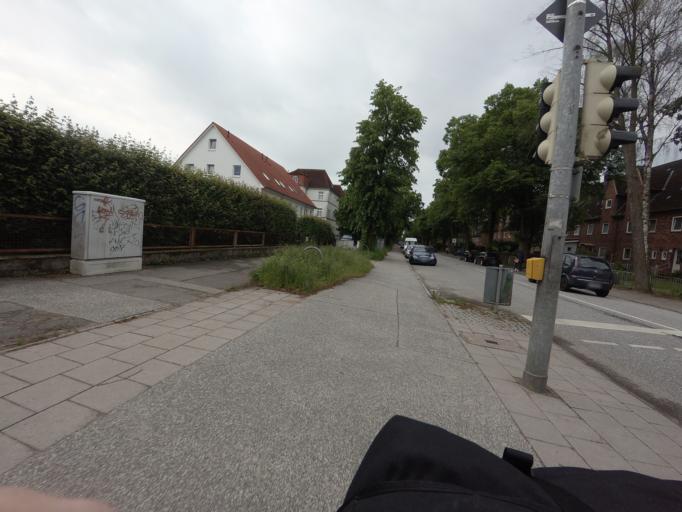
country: DE
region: Mecklenburg-Vorpommern
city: Selmsdorf
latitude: 53.9054
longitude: 10.8032
